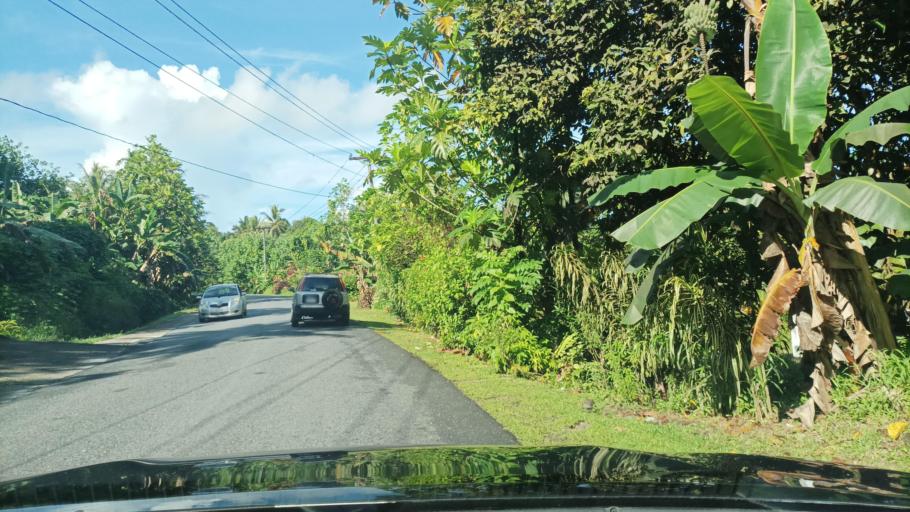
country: FM
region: Pohnpei
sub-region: Kolonia Municipality
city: Kolonia Town
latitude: 6.9442
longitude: 158.1844
